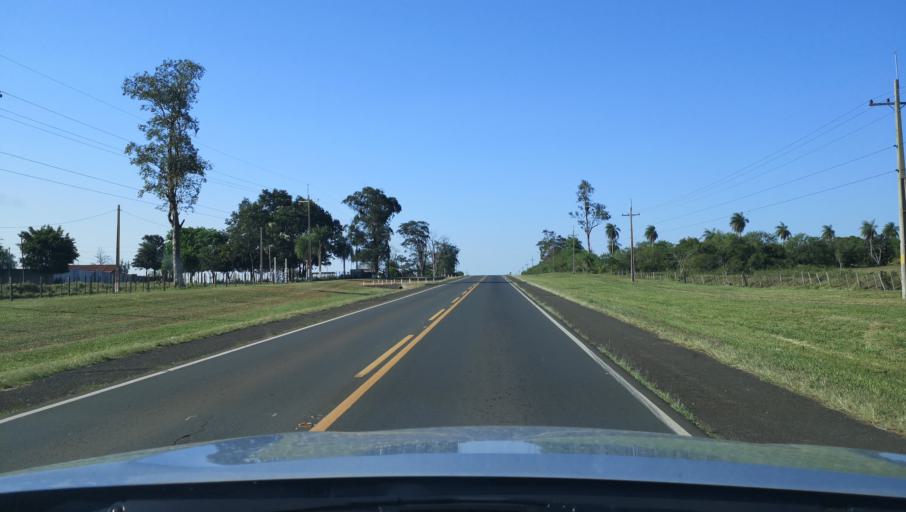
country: PY
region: Misiones
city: Santa Maria
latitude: -26.8247
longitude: -57.0283
